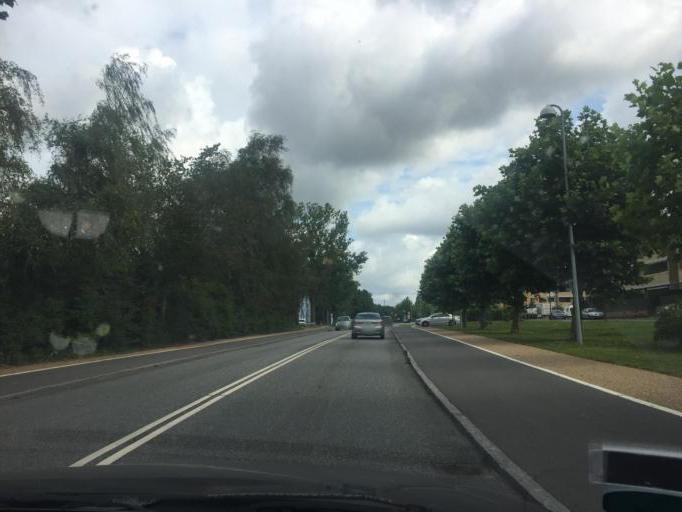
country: DK
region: Capital Region
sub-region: Allerod Kommune
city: Lillerod
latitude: 55.8791
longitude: 12.3506
